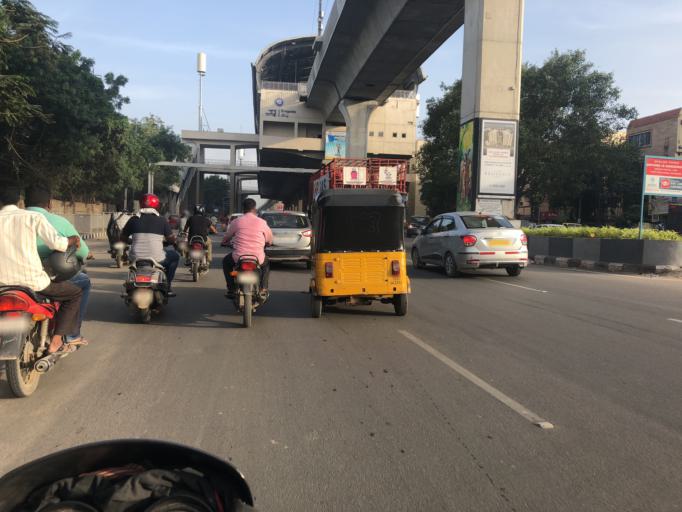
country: IN
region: Telangana
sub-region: Rangareddi
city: Kukatpalli
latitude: 17.4584
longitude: 78.4331
